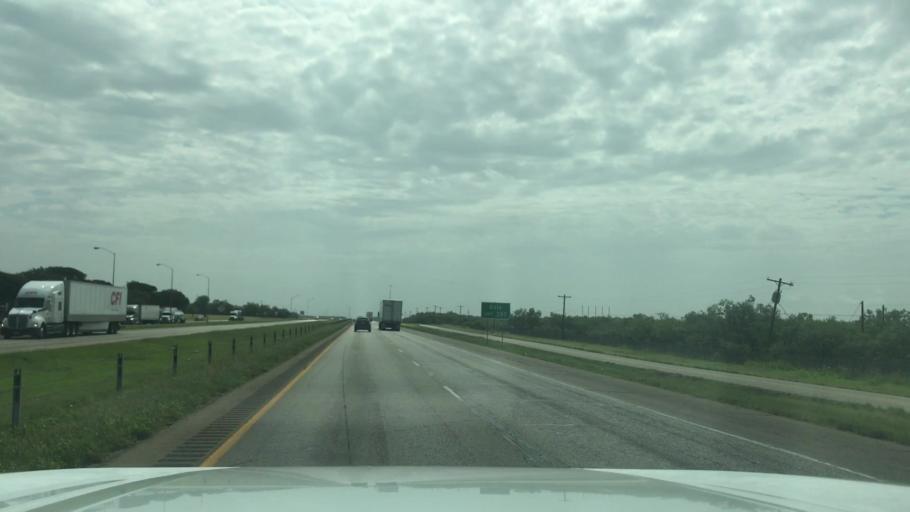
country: US
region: Texas
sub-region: Callahan County
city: Clyde
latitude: 32.4270
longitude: -99.5758
